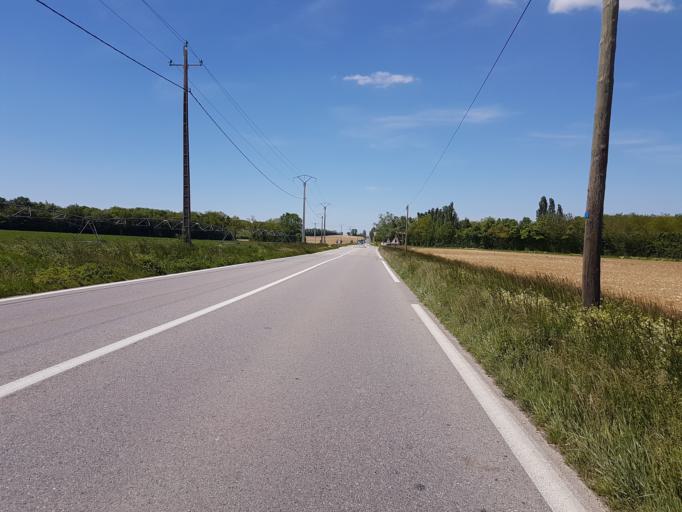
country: FR
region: Rhone-Alpes
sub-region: Departement de l'Isere
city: Chavanoz
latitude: 45.7850
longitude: 5.1492
